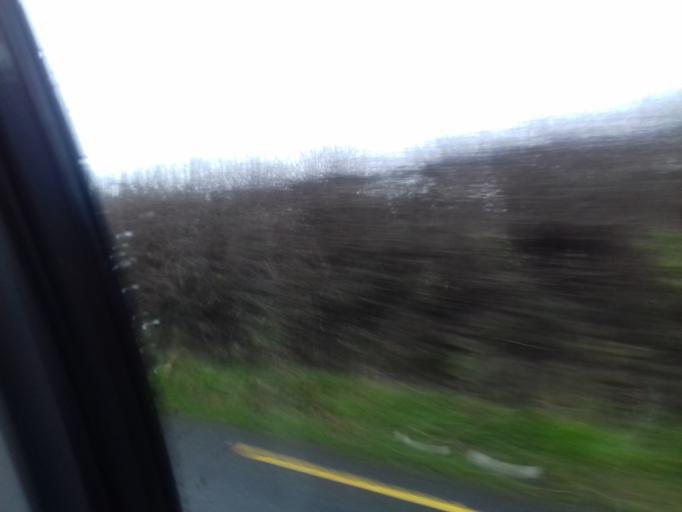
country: IE
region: Leinster
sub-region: Kilkenny
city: Graiguenamanagh
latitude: 52.5947
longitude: -6.9880
